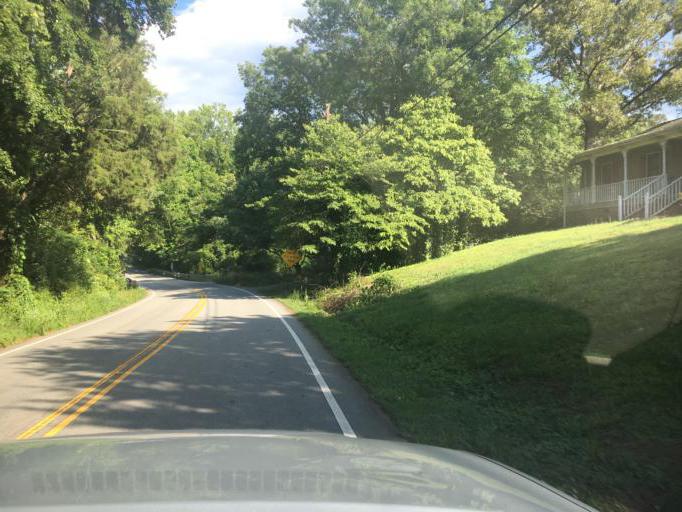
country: US
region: South Carolina
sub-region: Greenville County
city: Simpsonville
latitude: 34.7740
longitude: -82.2688
